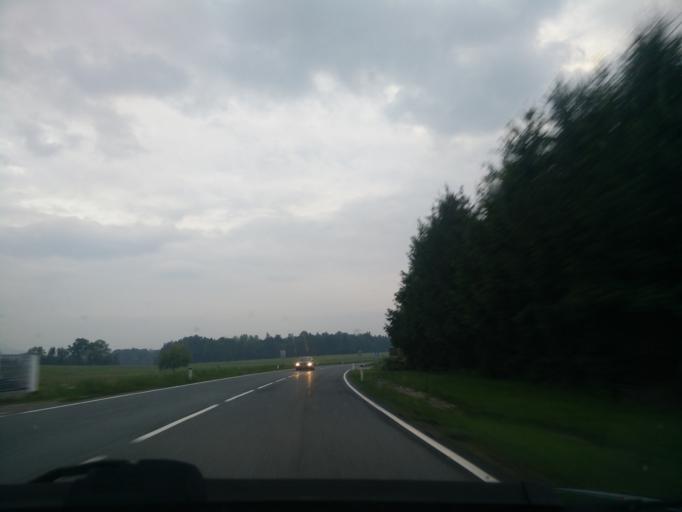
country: AT
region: Salzburg
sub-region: Politischer Bezirk Salzburg-Umgebung
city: Elixhausen
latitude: 47.8977
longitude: 13.0781
